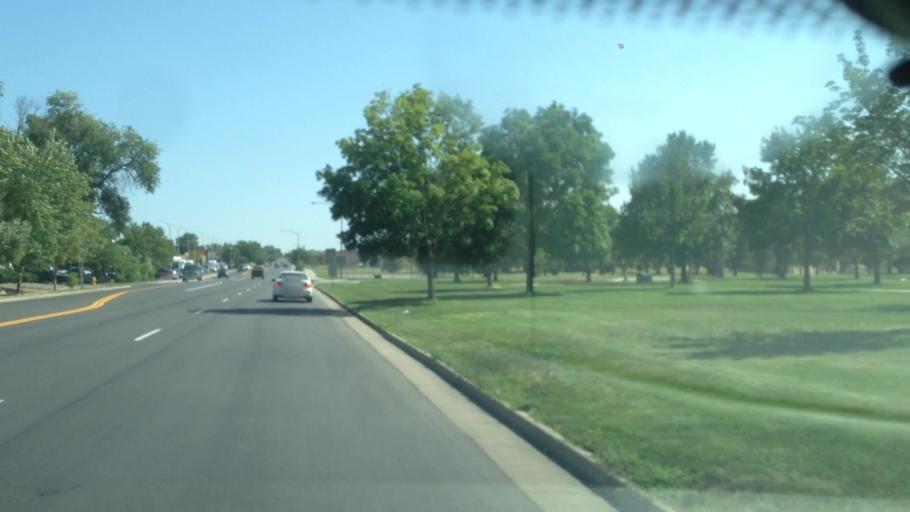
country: US
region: Colorado
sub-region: Adams County
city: Aurora
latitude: 39.7320
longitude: -104.8754
